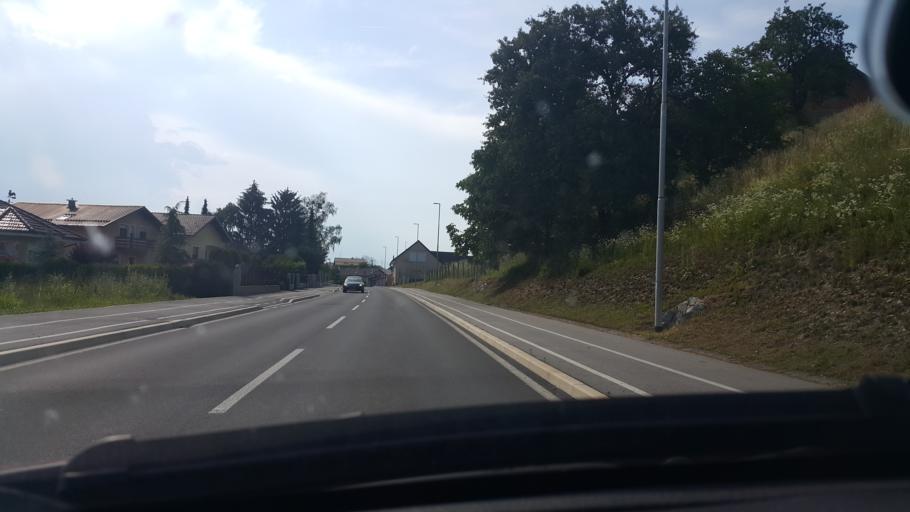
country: SI
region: Duplek
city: Spodnji Duplek
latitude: 46.5001
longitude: 15.7583
